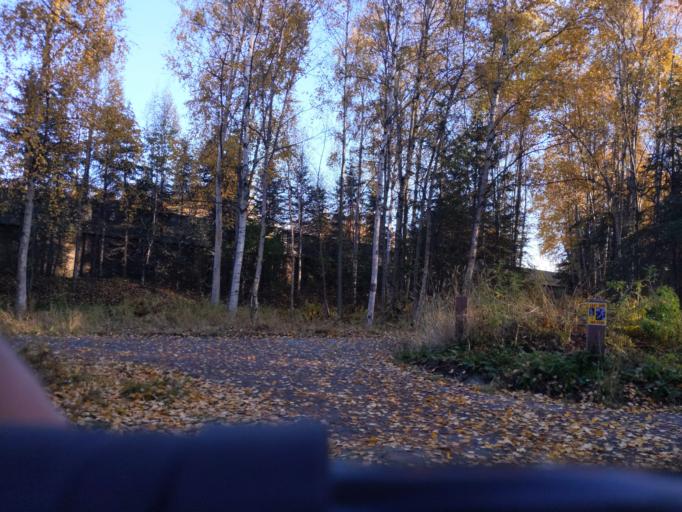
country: US
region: Alaska
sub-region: Anchorage Municipality
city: Anchorage
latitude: 61.1479
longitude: -149.8882
